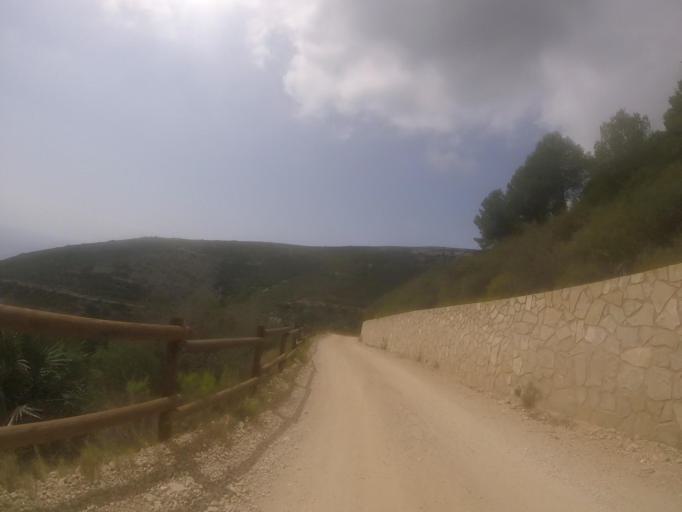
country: ES
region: Valencia
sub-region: Provincia de Castello
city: Peniscola
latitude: 40.3471
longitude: 0.3566
